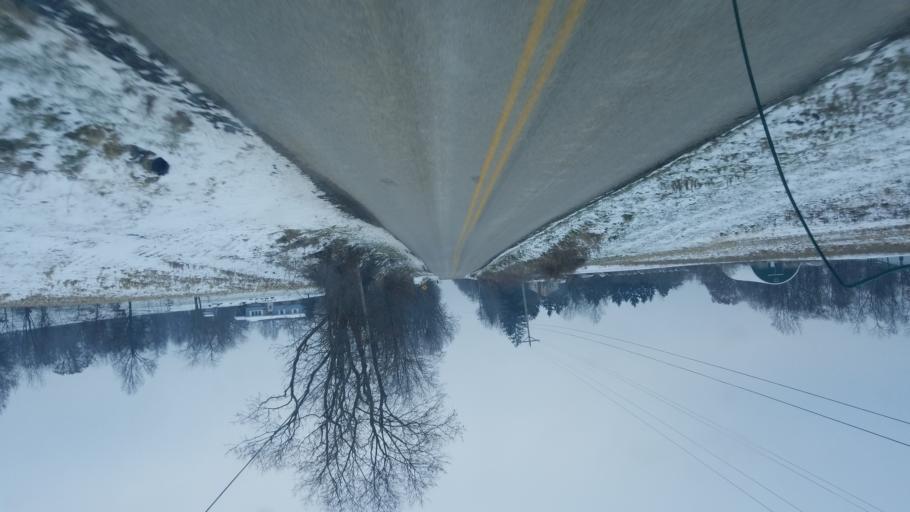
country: US
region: Ohio
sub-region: Richland County
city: Lincoln Heights
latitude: 40.6854
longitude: -82.4167
